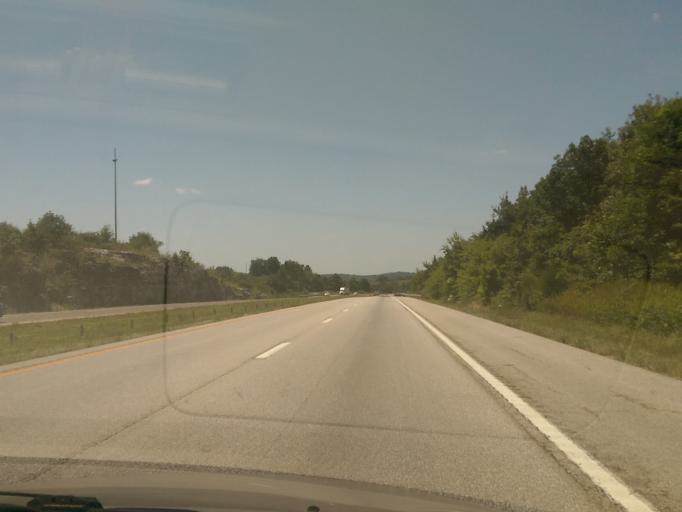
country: US
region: Missouri
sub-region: Cooper County
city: Boonville
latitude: 38.9335
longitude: -92.9687
